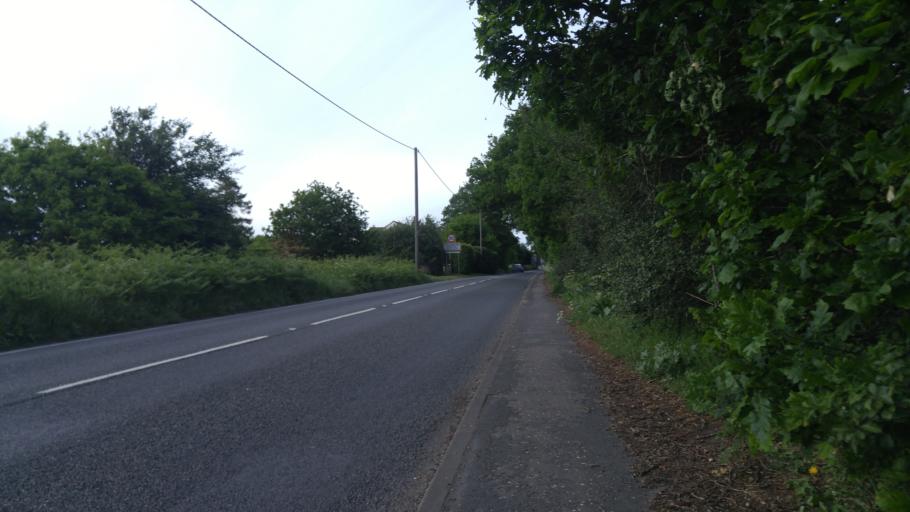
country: GB
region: England
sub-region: Essex
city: Layer de la Haye
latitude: 51.8621
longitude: 0.8693
